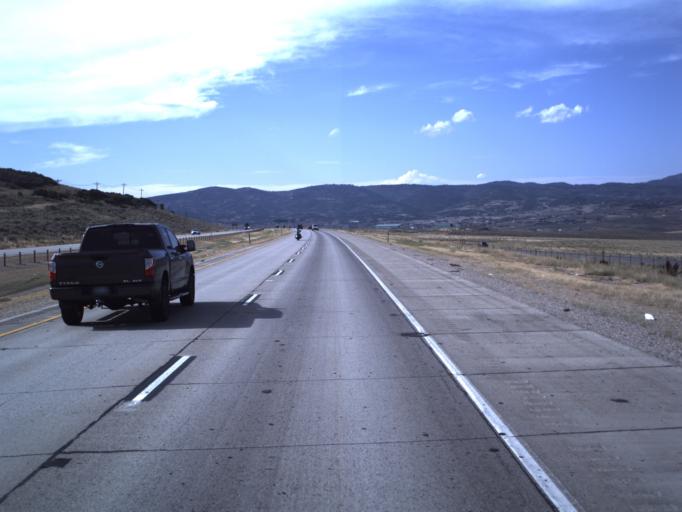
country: US
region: Utah
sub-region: Summit County
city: Park City
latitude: 40.6998
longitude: -111.4733
